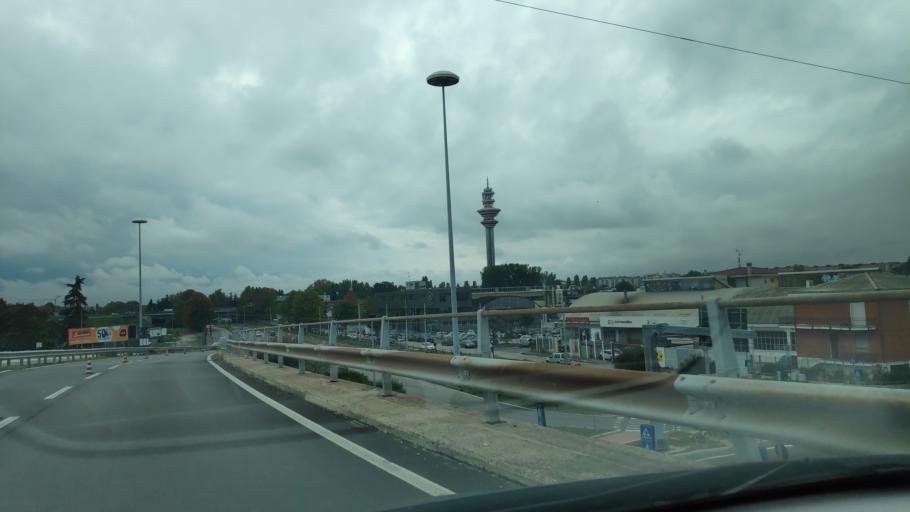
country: IT
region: Lombardy
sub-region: Citta metropolitana di Milano
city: Rozzano
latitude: 45.3895
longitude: 9.1727
